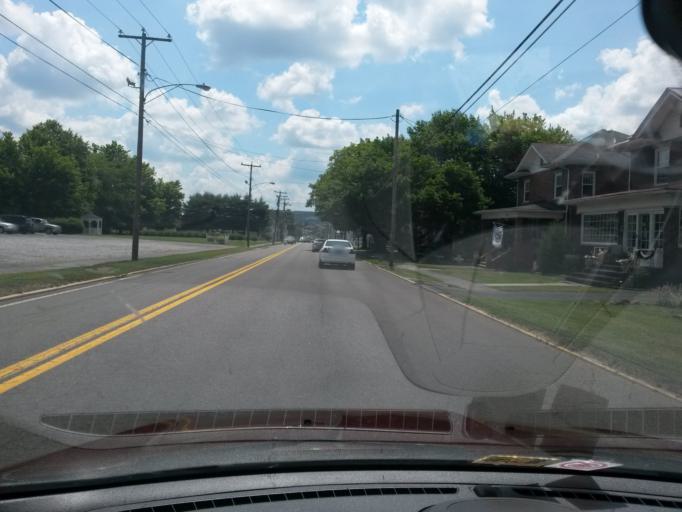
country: US
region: West Virginia
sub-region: Mercer County
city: Princeton
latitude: 37.3676
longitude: -81.1046
